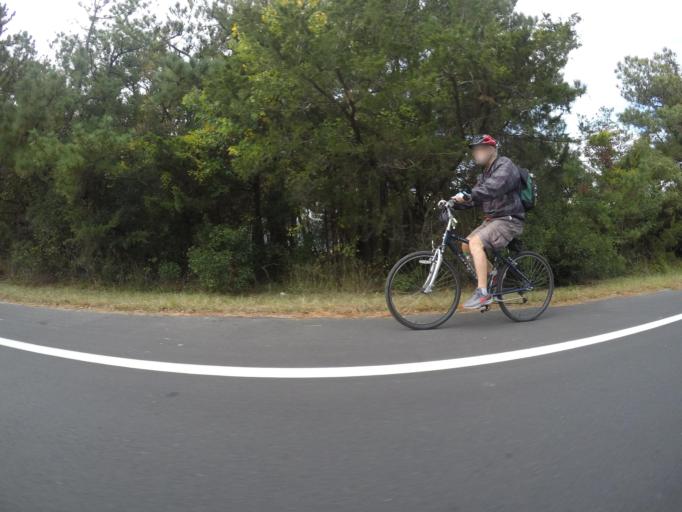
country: US
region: Delaware
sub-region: Sussex County
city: Rehoboth Beach
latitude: 38.7277
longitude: -75.0795
